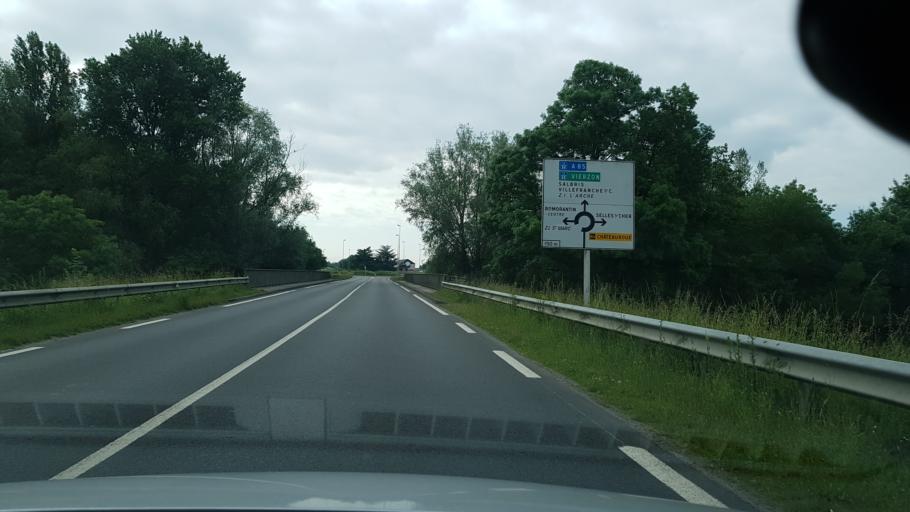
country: FR
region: Centre
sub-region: Departement du Loir-et-Cher
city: Romorantin-Lanthenay
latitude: 47.3481
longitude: 1.7259
